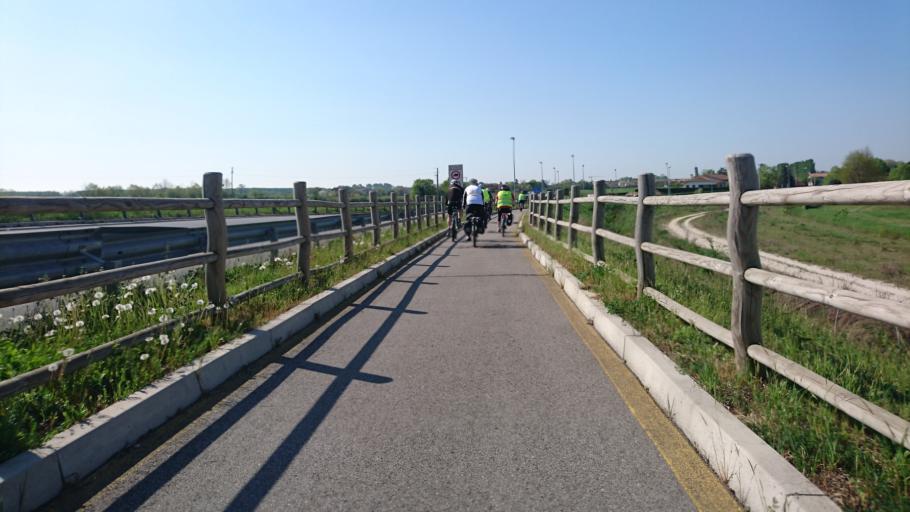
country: IT
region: Veneto
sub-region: Provincia di Treviso
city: Musestre
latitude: 45.5940
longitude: 12.3785
